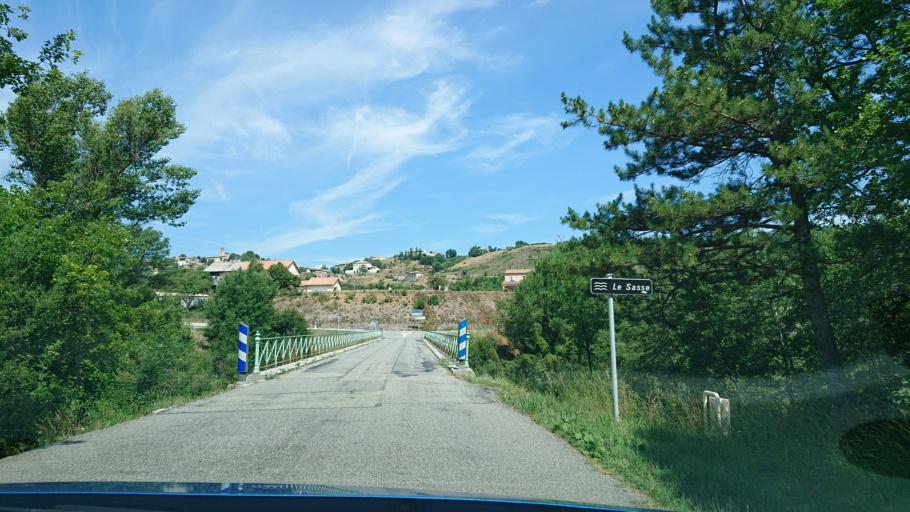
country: FR
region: Provence-Alpes-Cote d'Azur
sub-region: Departement des Alpes-de-Haute-Provence
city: Sisteron
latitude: 44.2571
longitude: 5.9661
